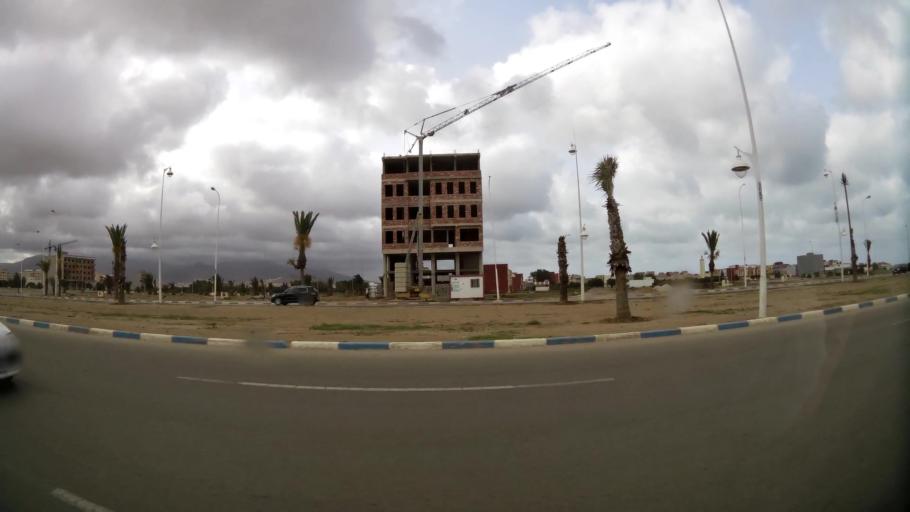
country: MA
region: Oriental
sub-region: Nador
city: Nador
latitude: 35.1531
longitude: -2.9170
